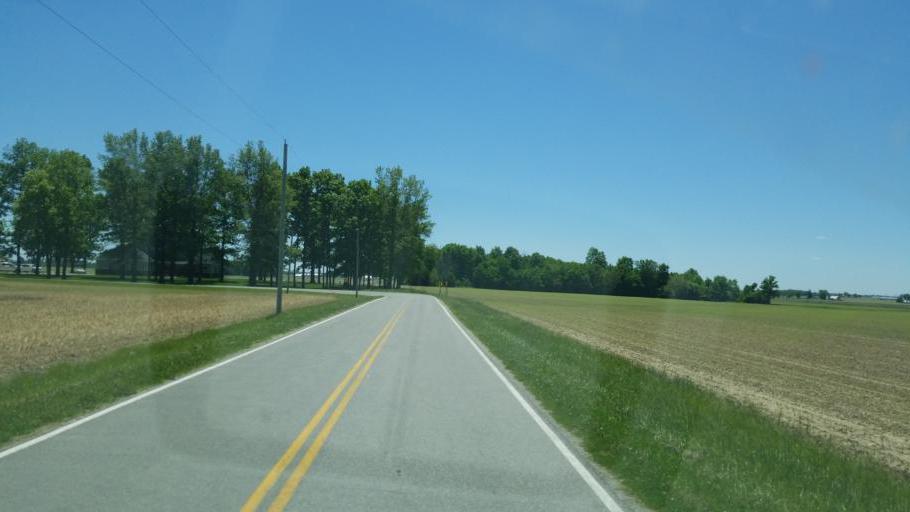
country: US
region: Ohio
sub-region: Darke County
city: Union City
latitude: 40.2806
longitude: -84.7285
